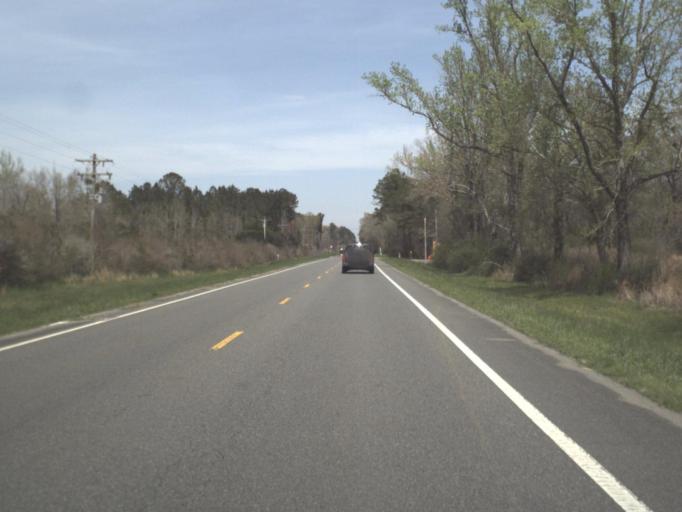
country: US
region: Florida
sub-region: Walton County
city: DeFuniak Springs
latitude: 30.7716
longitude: -85.9588
